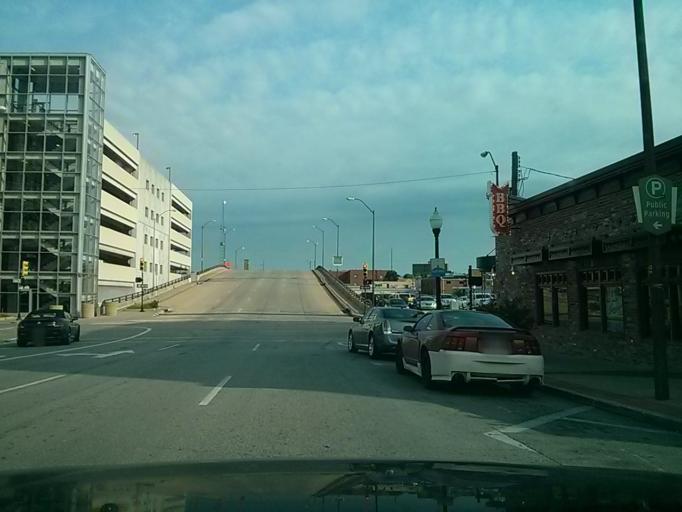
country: US
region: Oklahoma
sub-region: Tulsa County
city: Tulsa
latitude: 36.1562
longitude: -95.9883
